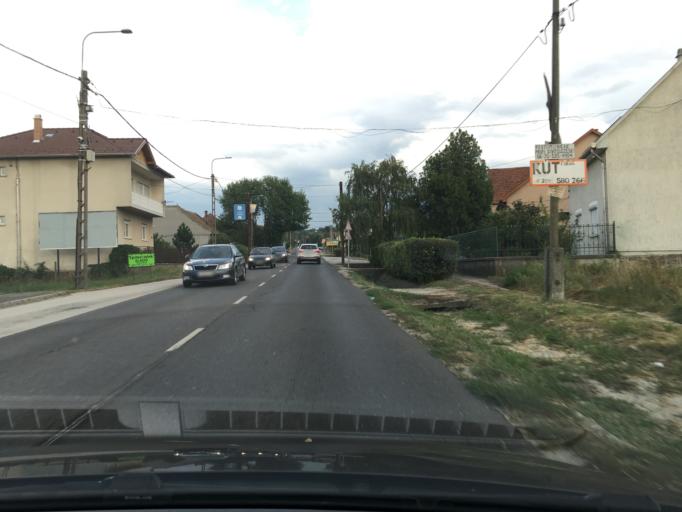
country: HU
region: Pest
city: Veresegyhaz
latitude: 47.6415
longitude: 19.3020
